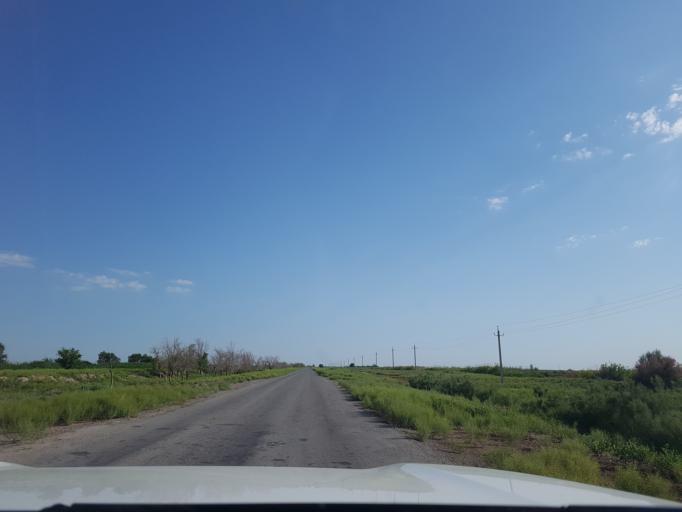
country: TM
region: Dasoguz
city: Koeneuergench
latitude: 41.8889
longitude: 58.7069
